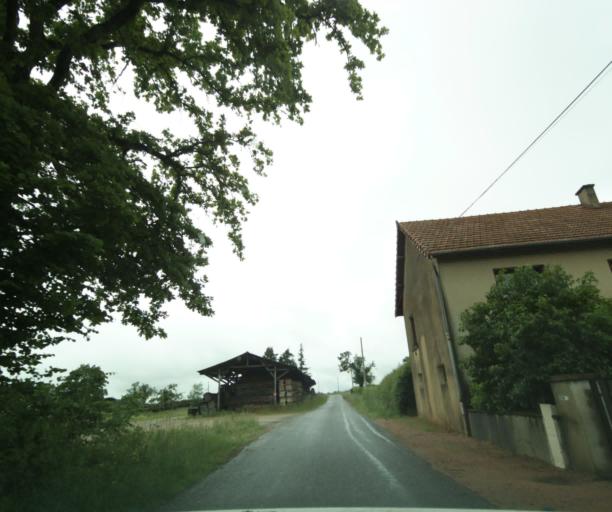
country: FR
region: Bourgogne
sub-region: Departement de Saone-et-Loire
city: Charolles
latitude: 46.4496
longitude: 4.3289
